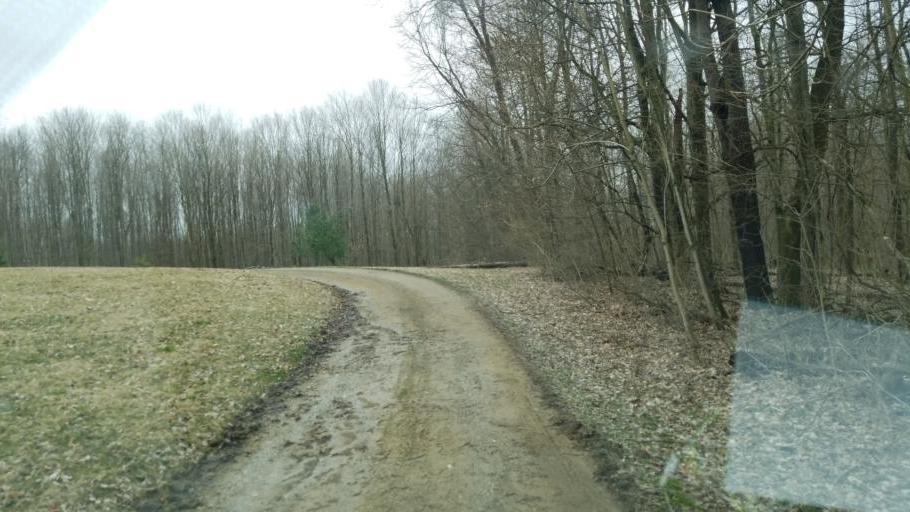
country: US
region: Ohio
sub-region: Knox County
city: Mount Vernon
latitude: 40.4584
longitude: -82.4316
